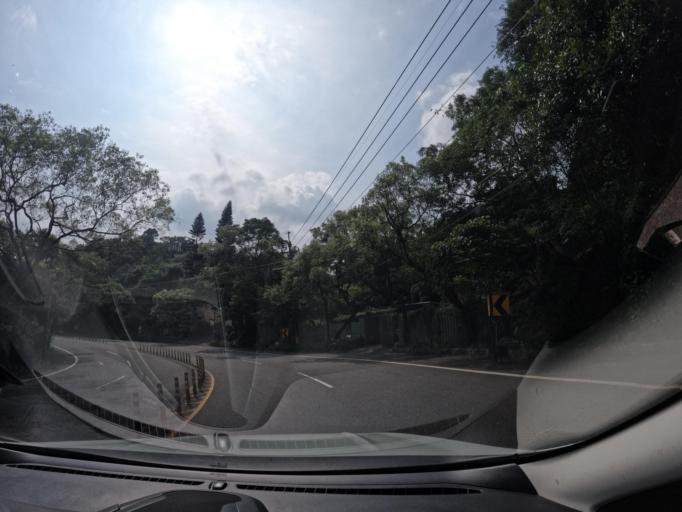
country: TW
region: Taiwan
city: Daxi
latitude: 24.8964
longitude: 121.3329
